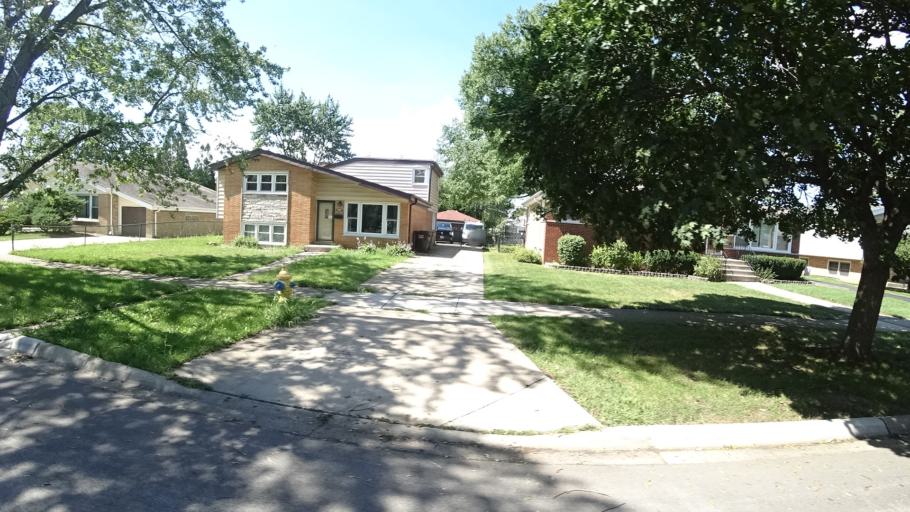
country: US
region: Illinois
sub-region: Cook County
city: Tinley Park
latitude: 41.5706
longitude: -87.7886
